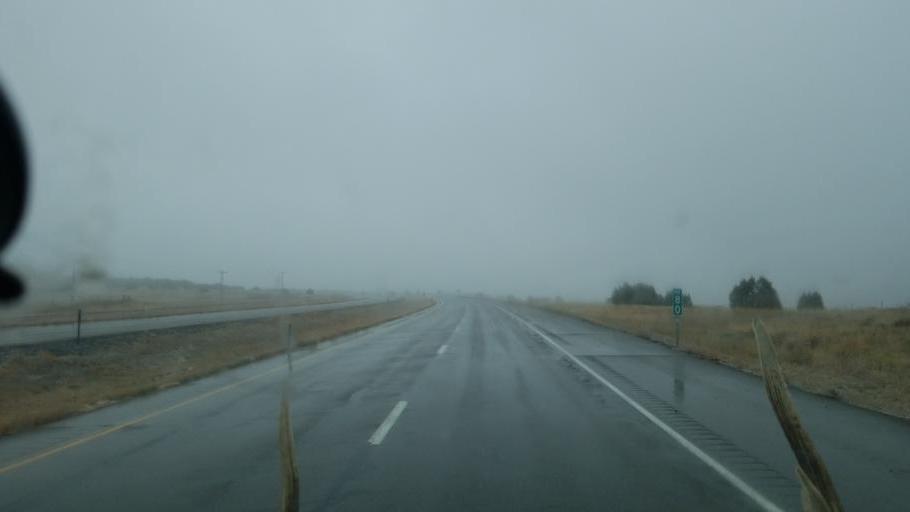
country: US
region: Colorado
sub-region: Pueblo County
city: Colorado City
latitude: 38.0267
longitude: -104.7334
